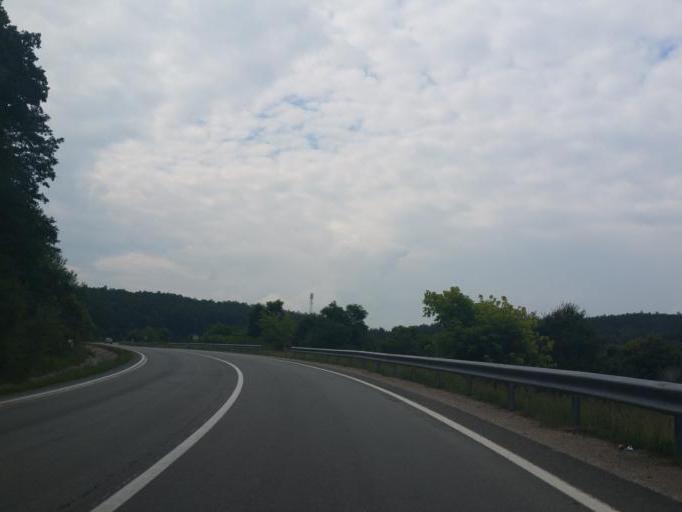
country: RO
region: Salaj
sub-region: Comuna Romanasi
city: Romanasi
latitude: 47.0668
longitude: 23.2118
